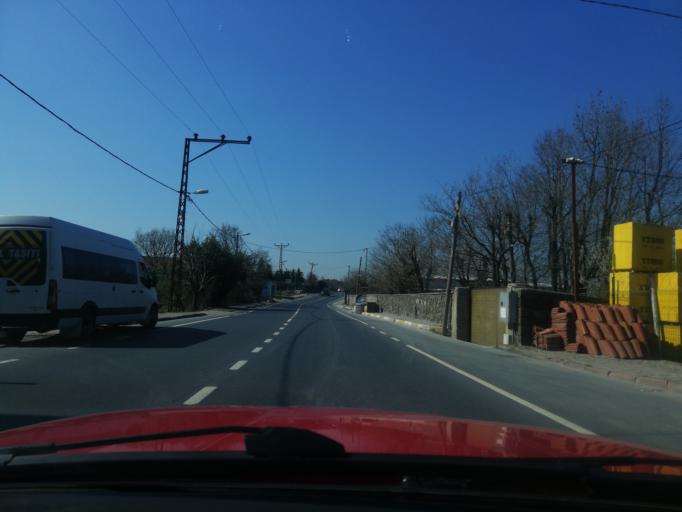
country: TR
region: Istanbul
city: Umraniye
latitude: 41.0707
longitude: 29.1615
